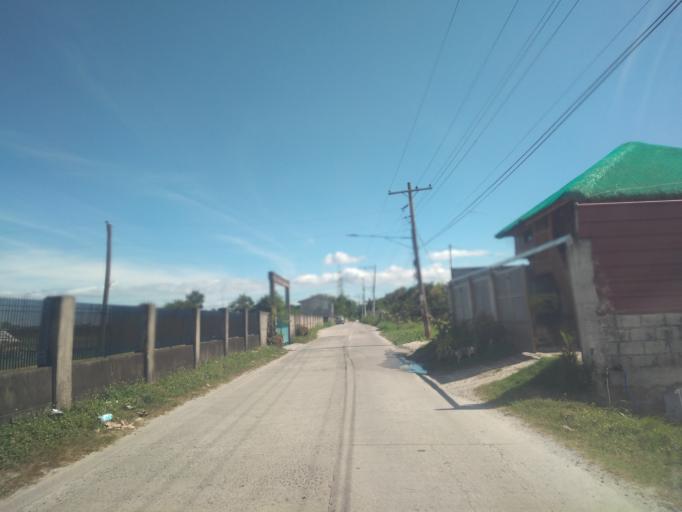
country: PH
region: Central Luzon
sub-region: Province of Pampanga
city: Bacolor
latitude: 15.0085
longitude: 120.6458
